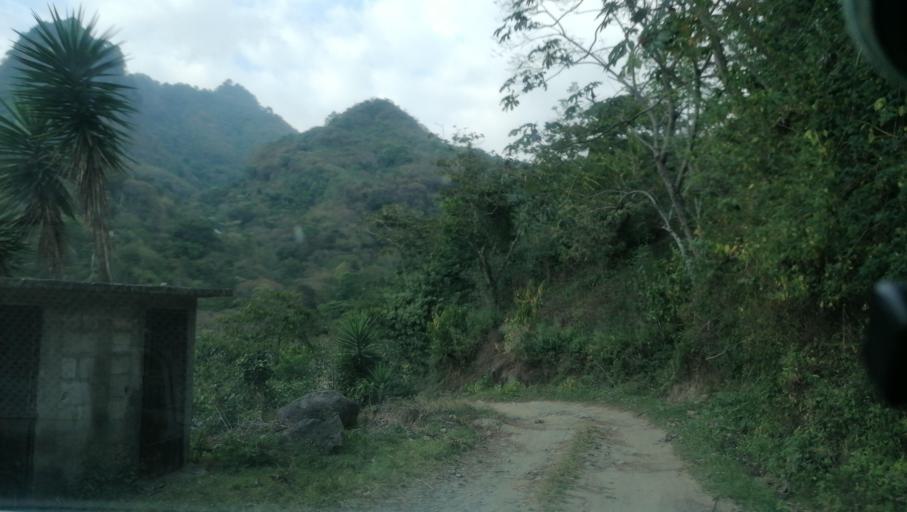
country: MX
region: Chiapas
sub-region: Cacahoatan
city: Benito Juarez
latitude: 15.1434
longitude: -92.1914
